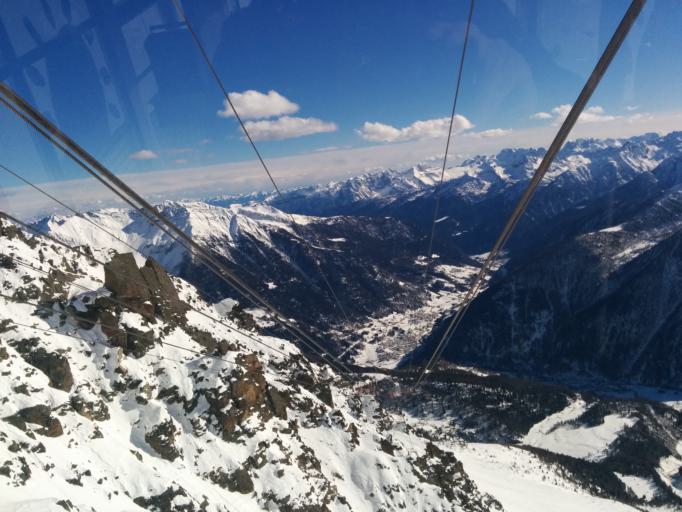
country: IT
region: Trentino-Alto Adige
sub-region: Provincia di Trento
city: Cogolo
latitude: 46.3832
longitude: 10.6319
